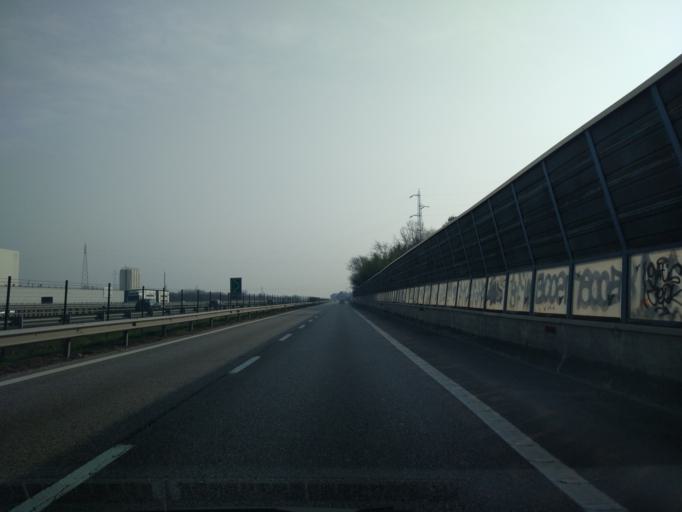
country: IT
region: Veneto
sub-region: Provincia di Verona
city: San Giovanni Lupatoto
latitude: 45.4004
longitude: 11.0187
